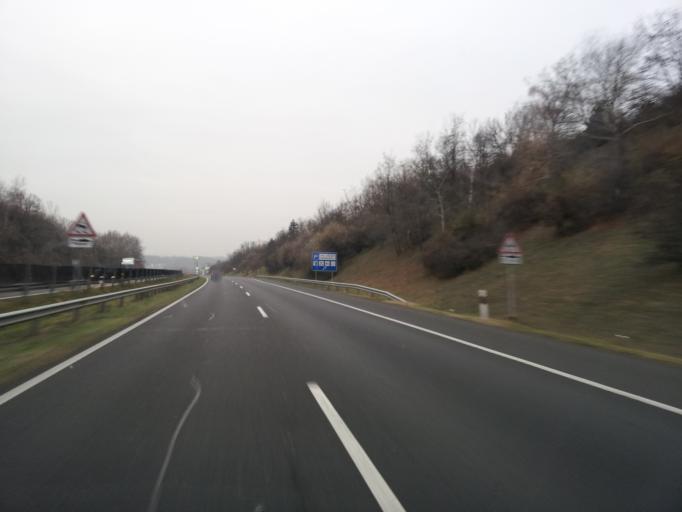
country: HU
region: Fejer
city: Baracska
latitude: 47.3120
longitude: 18.7482
